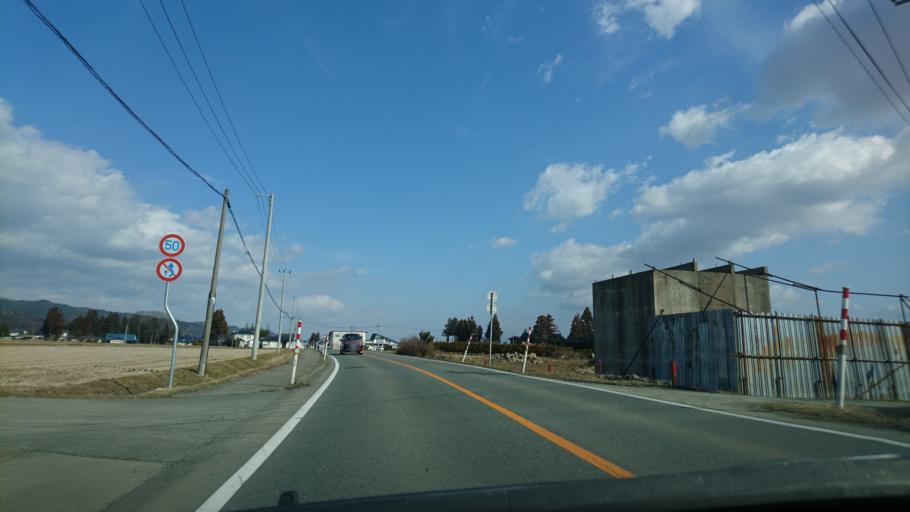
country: JP
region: Iwate
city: Morioka-shi
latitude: 39.5615
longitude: 141.1083
